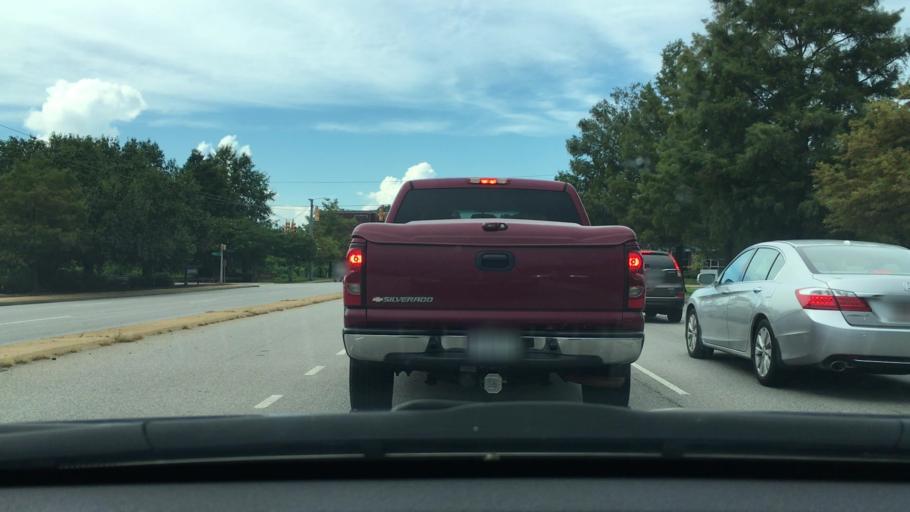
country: US
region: South Carolina
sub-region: Richland County
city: Columbia
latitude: 34.0051
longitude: -81.0481
